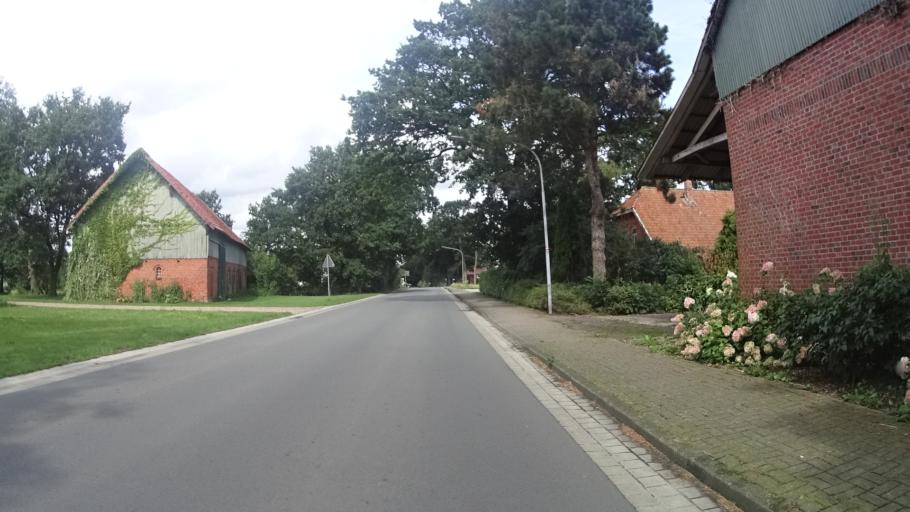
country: DE
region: Lower Saxony
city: Mittelstenahe
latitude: 53.6524
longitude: 9.0342
